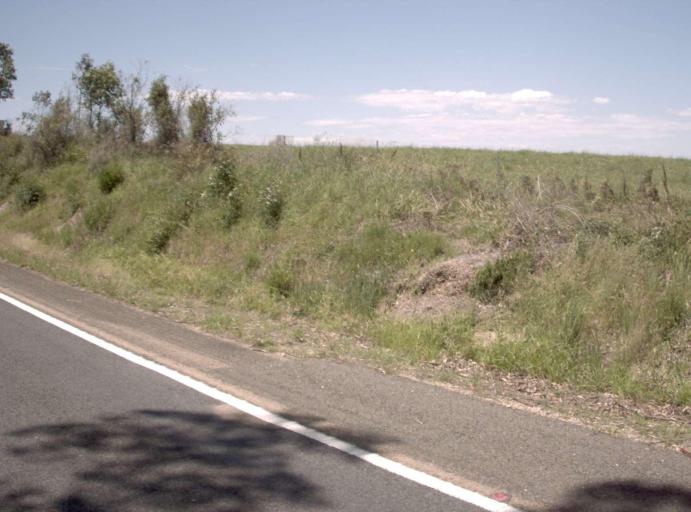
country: AU
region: Victoria
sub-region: East Gippsland
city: Lakes Entrance
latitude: -37.7044
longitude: 148.5145
